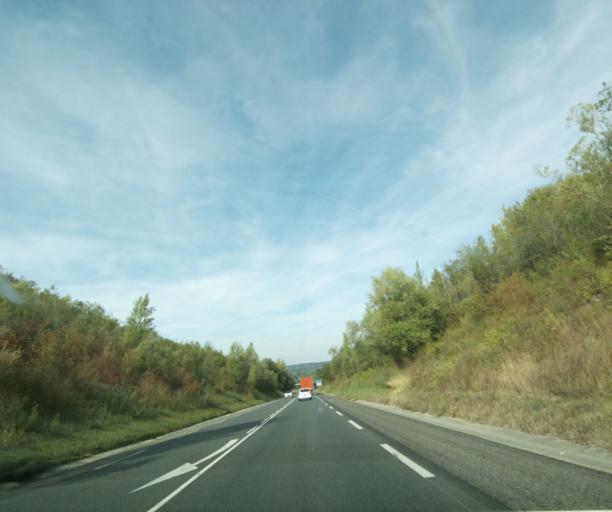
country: FR
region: Auvergne
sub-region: Departement de l'Allier
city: Saint-Germain-des-Fosses
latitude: 46.1907
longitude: 3.4343
